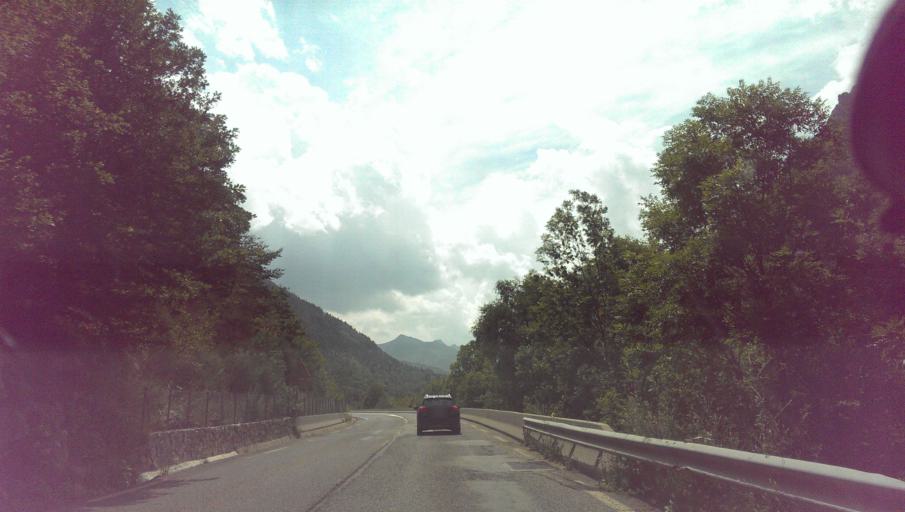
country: AD
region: Encamp
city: Pas de la Casa
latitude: 42.6043
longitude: 1.8131
